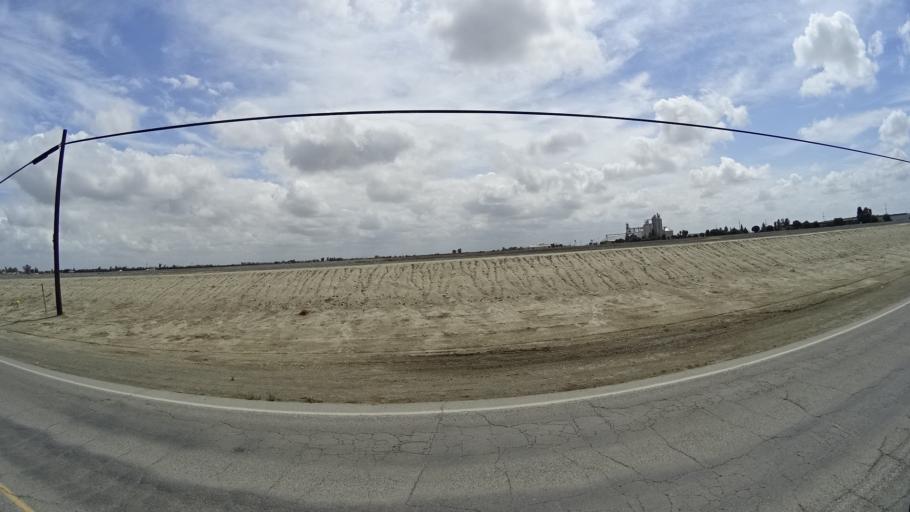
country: US
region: California
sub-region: Kings County
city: Home Garden
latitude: 36.2868
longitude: -119.6549
